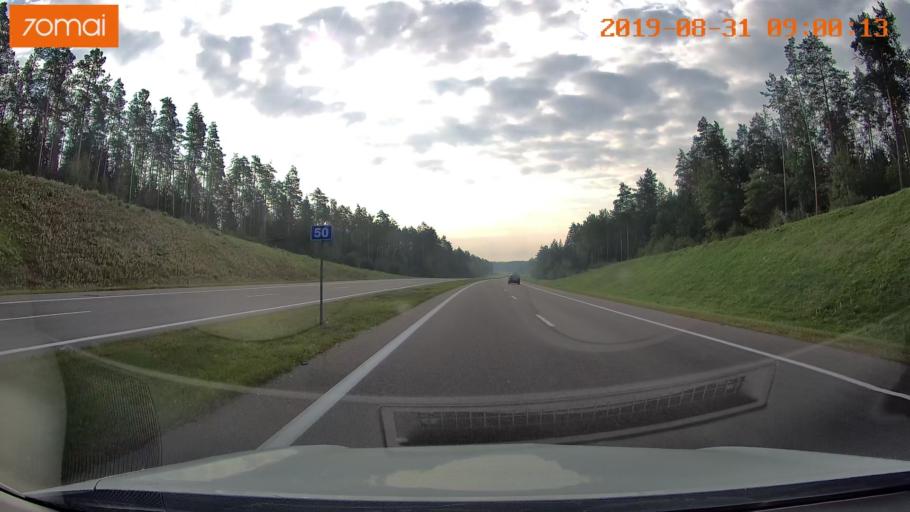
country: BY
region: Minsk
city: Chervyen'
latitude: 53.7605
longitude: 28.2311
